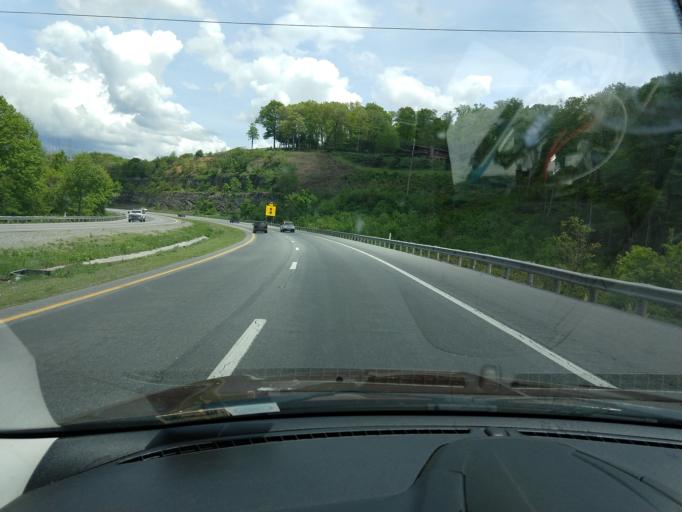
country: US
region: West Virginia
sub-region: Mercer County
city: Princeton
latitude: 37.3542
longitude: -81.1021
